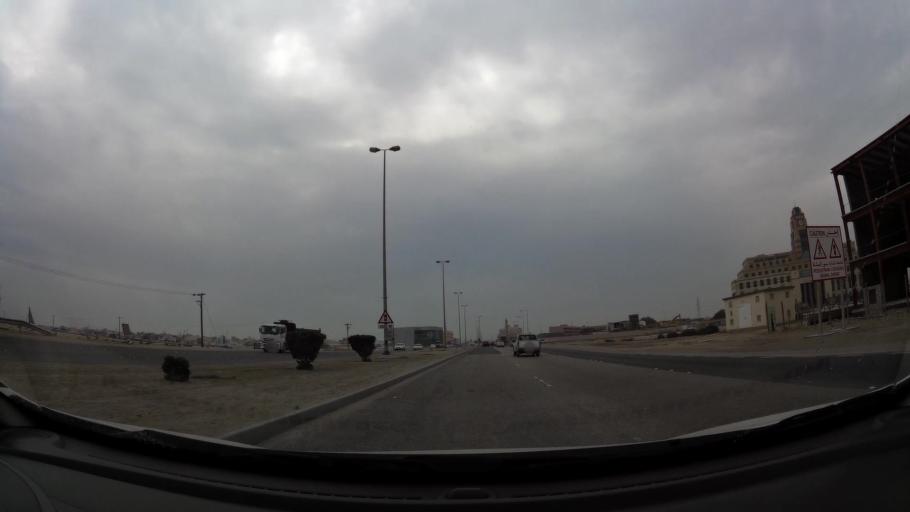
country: BH
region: Northern
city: Sitrah
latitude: 26.1426
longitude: 50.6173
